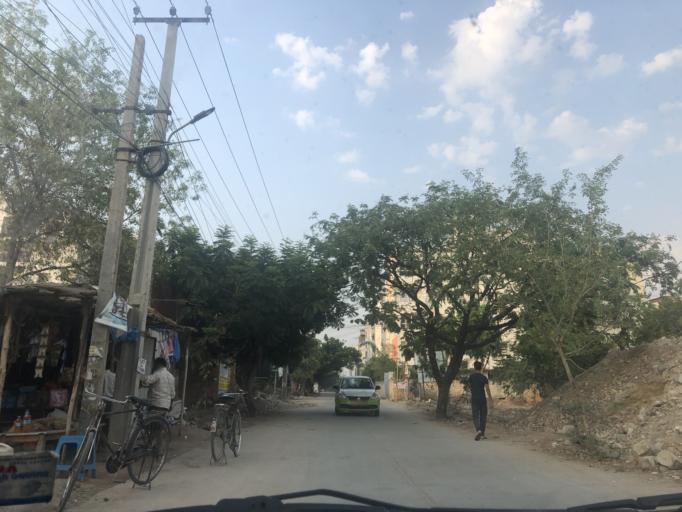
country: IN
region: Telangana
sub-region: Rangareddi
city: Kukatpalli
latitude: 17.4445
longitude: 78.3988
